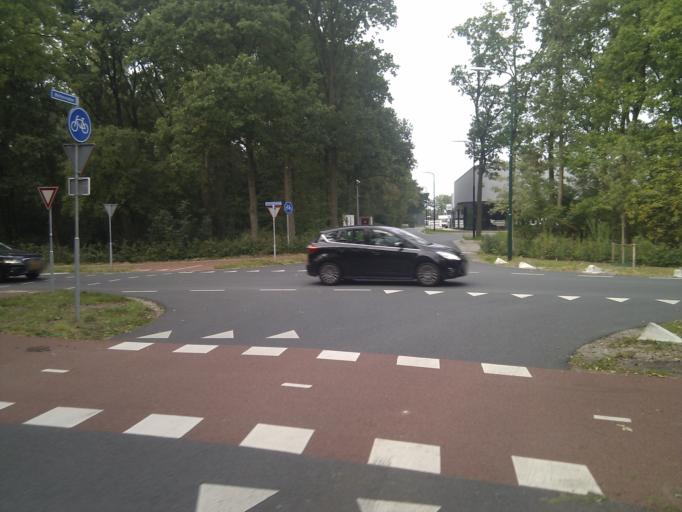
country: NL
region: Utrecht
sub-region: Gemeente De Bilt
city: De Bilt
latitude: 52.1163
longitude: 5.1743
